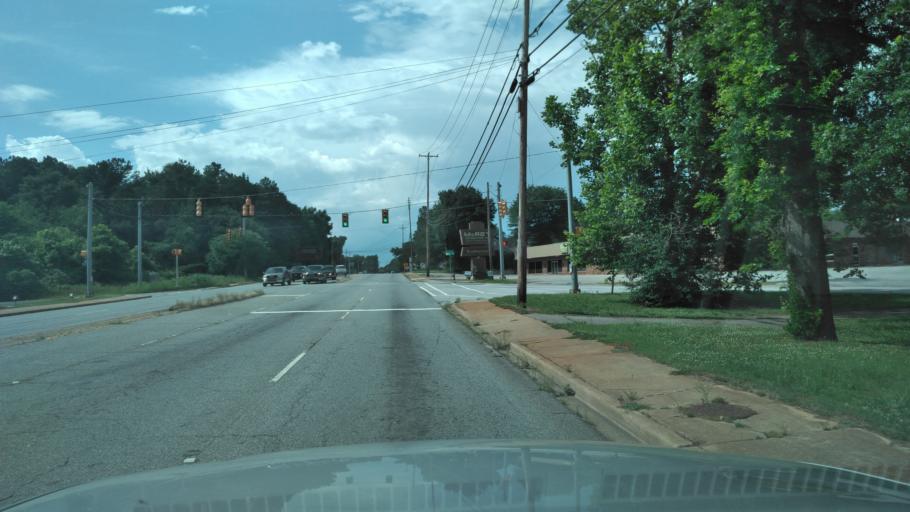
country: US
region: South Carolina
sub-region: Spartanburg County
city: Saxon
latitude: 34.9793
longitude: -81.9434
